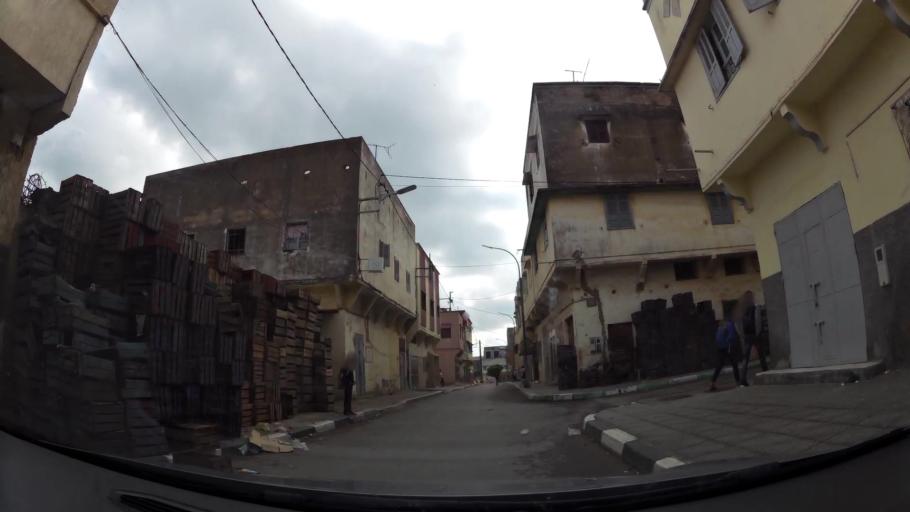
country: MA
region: Rabat-Sale-Zemmour-Zaer
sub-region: Khemisset
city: Tiflet
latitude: 33.8950
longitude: -6.3098
